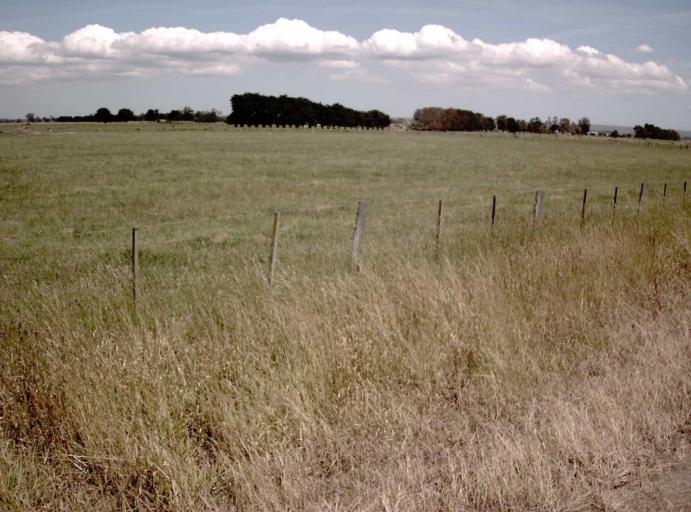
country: AU
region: Victoria
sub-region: Wellington
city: Heyfield
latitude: -38.0654
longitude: 146.8718
